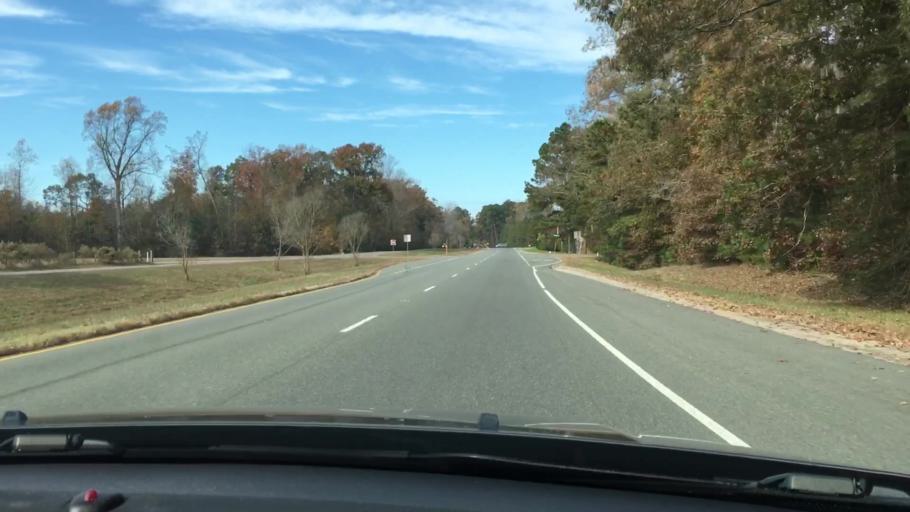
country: US
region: Virginia
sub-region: King William County
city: West Point
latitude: 37.4256
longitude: -76.8273
